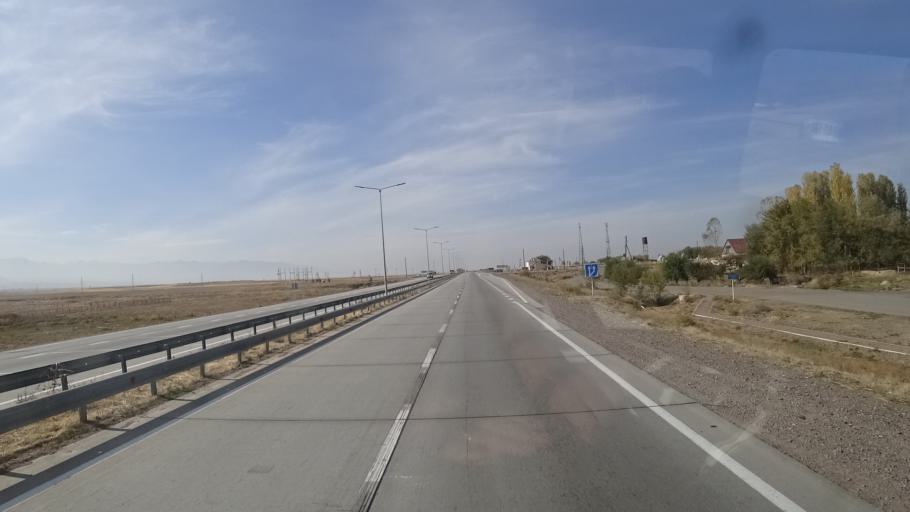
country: KZ
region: Zhambyl
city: Merke
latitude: 42.8889
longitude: 72.9908
